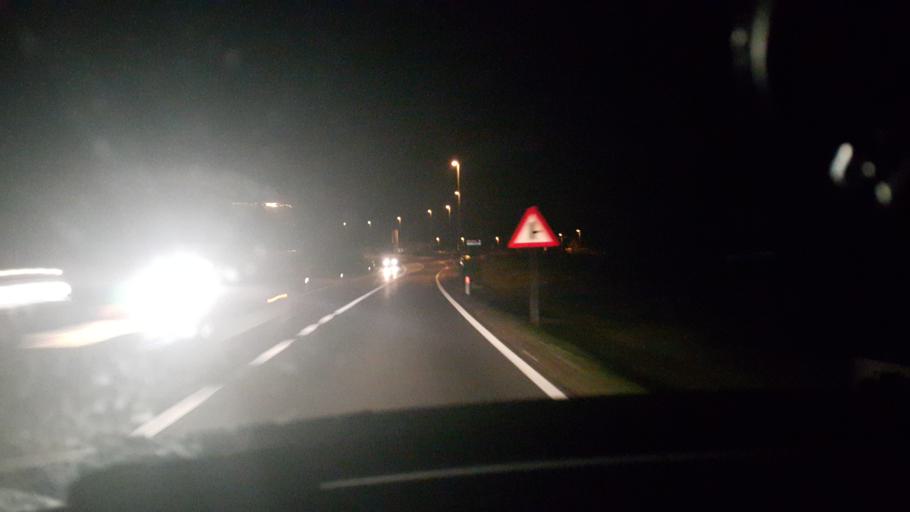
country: SI
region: Selnica ob Dravi
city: Selnica ob Dravi
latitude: 46.5610
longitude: 15.4580
